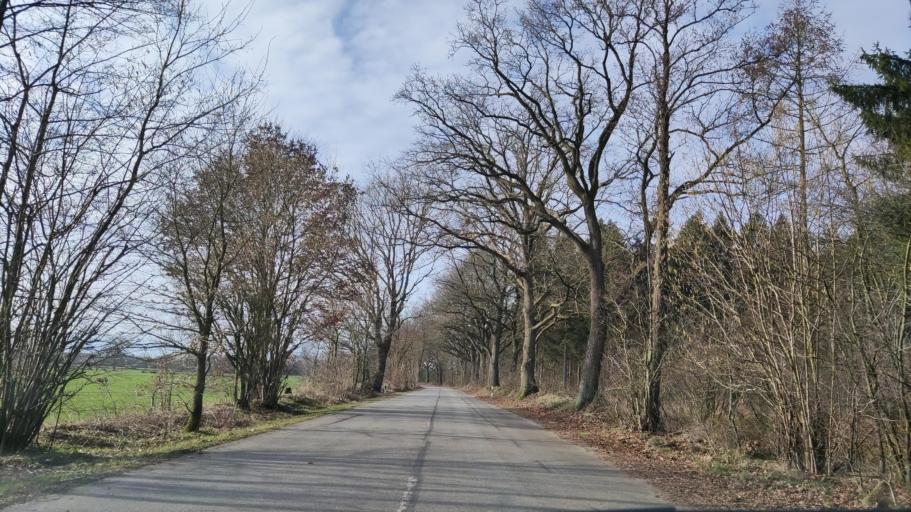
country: DE
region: Schleswig-Holstein
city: Schackendorf
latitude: 53.9692
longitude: 10.2727
